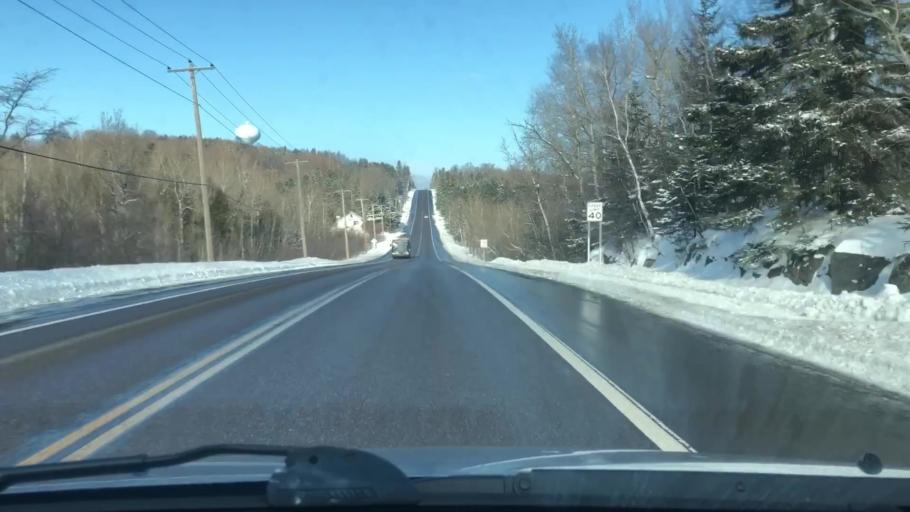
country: US
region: Minnesota
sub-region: Saint Louis County
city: Duluth
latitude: 46.8071
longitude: -92.1321
